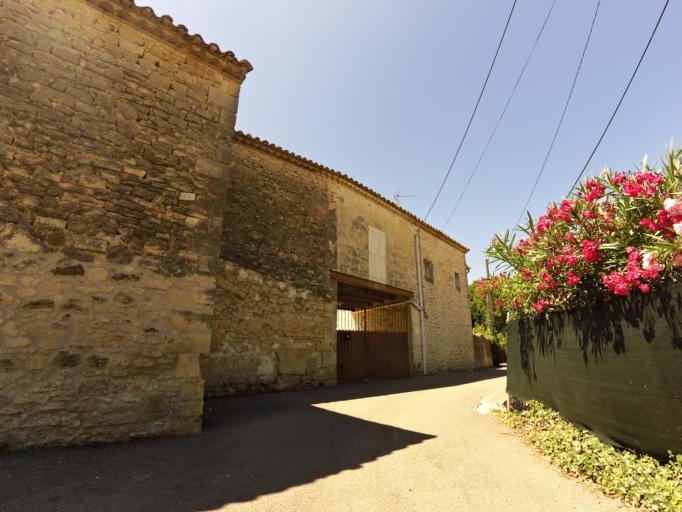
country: FR
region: Languedoc-Roussillon
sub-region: Departement du Gard
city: Aigues-Vives
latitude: 43.7408
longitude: 4.1682
